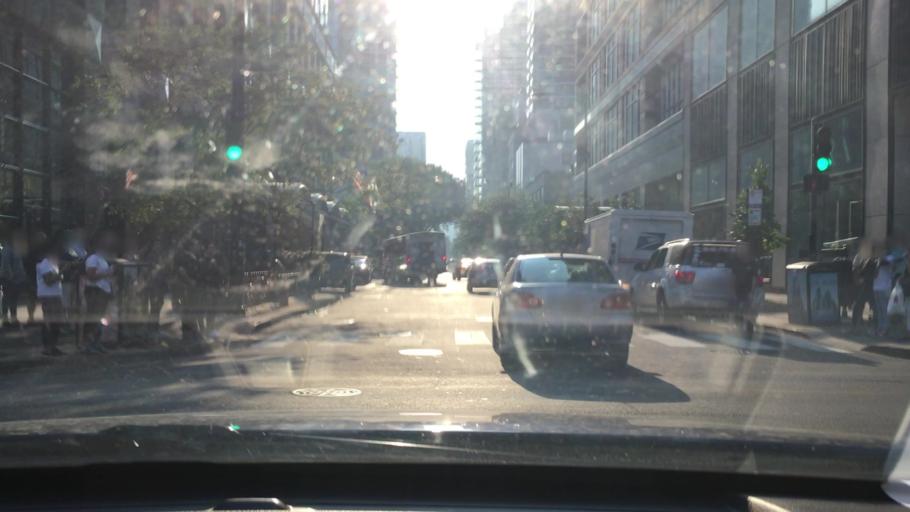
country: US
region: Illinois
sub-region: Cook County
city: Chicago
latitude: 41.8948
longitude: -87.6244
